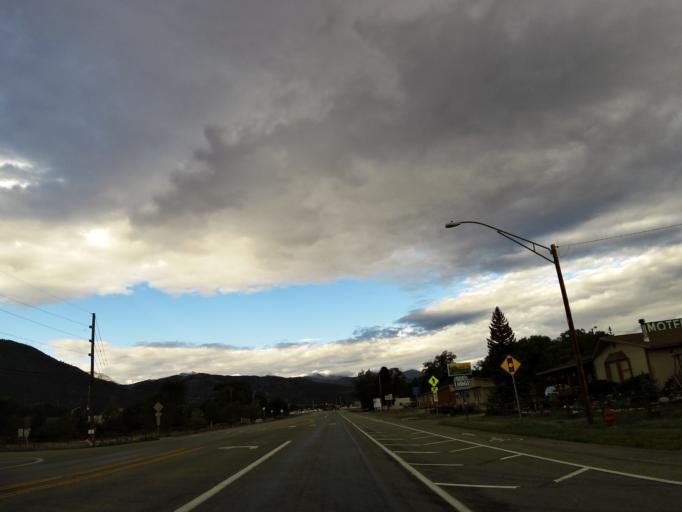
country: US
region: Colorado
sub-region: Chaffee County
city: Salida
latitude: 38.5154
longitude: -106.0713
